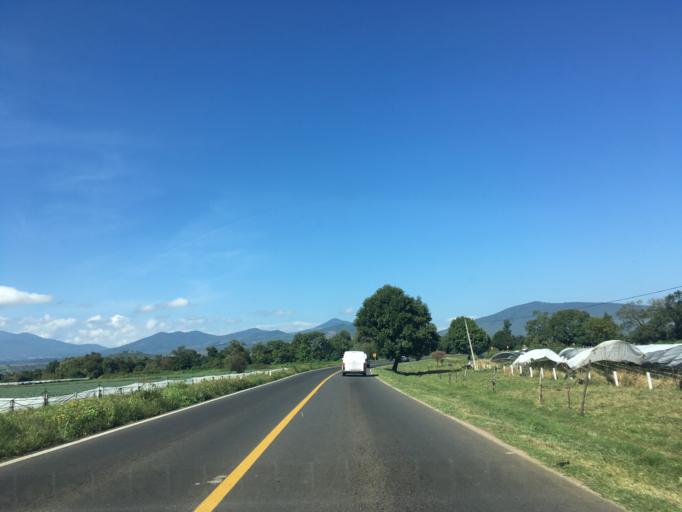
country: MX
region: Mexico
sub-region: Chalco
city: Los Nogales
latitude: 19.8610
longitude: -102.1844
